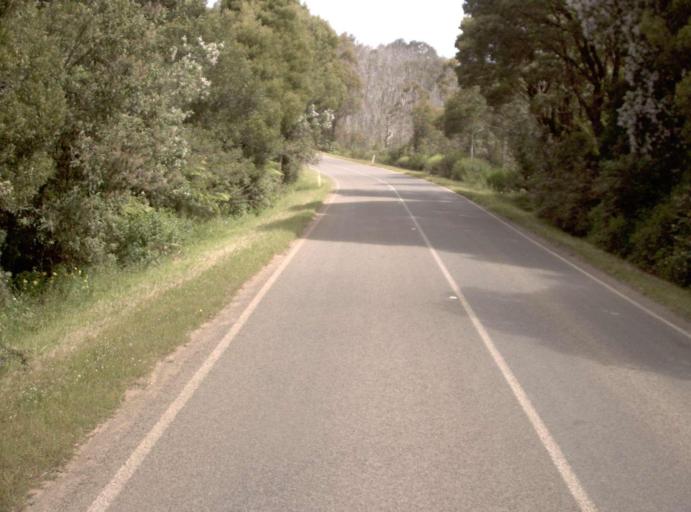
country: AU
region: Victoria
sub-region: Latrobe
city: Traralgon
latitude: -38.4122
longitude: 146.5658
